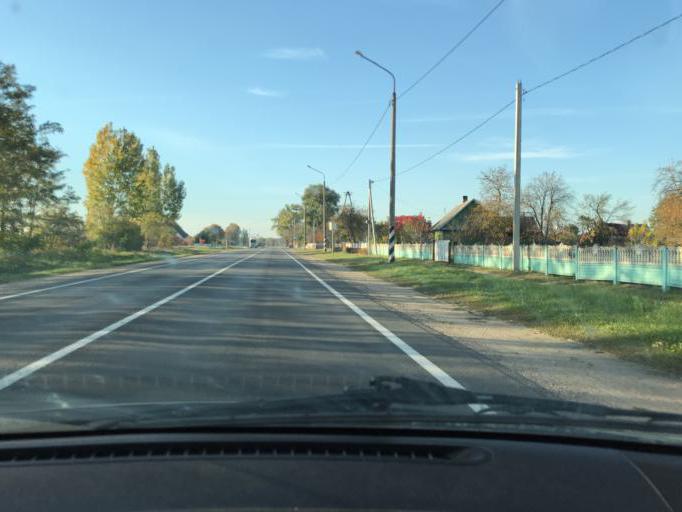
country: BY
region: Brest
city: Horad Kobryn
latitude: 52.2113
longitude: 24.5617
